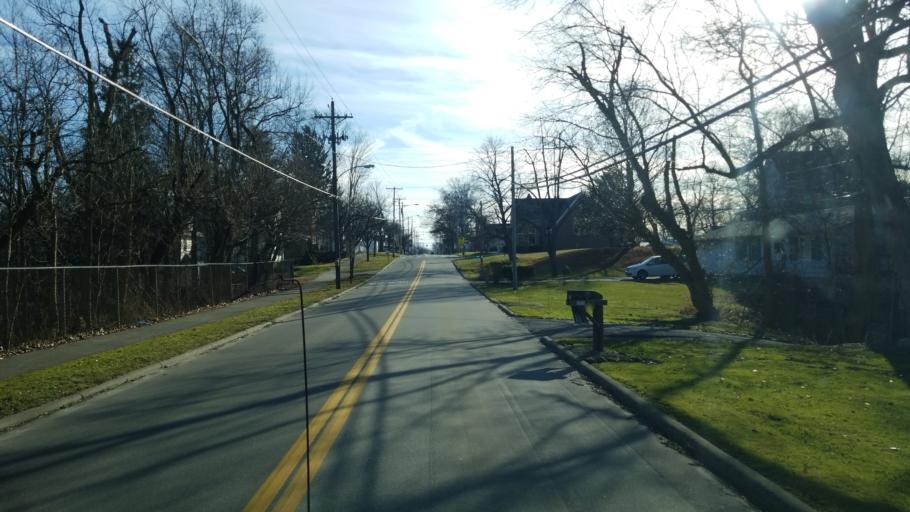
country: US
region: Ohio
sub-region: Sandusky County
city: Green Springs
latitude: 41.2601
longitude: -83.0520
